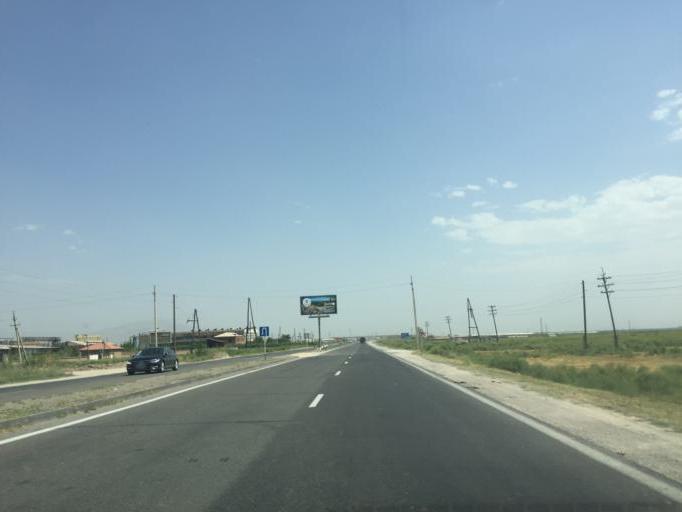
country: AM
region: Ararat
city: Shahumyan
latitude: 39.9380
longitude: 44.5597
